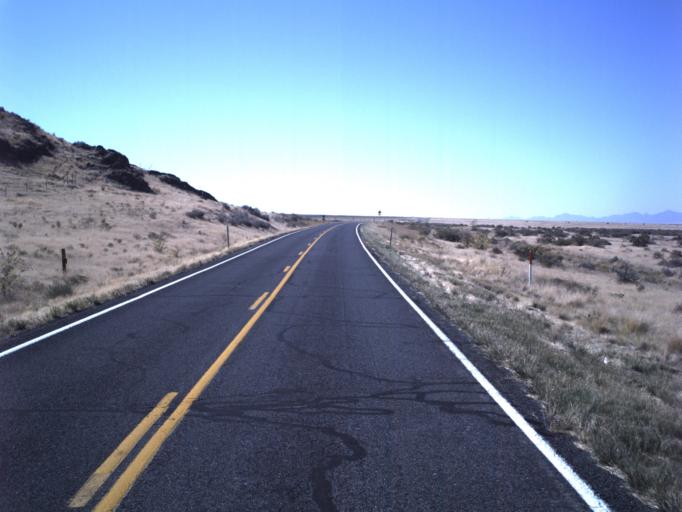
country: US
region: Utah
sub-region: Tooele County
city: Grantsville
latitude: 40.6124
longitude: -112.7050
